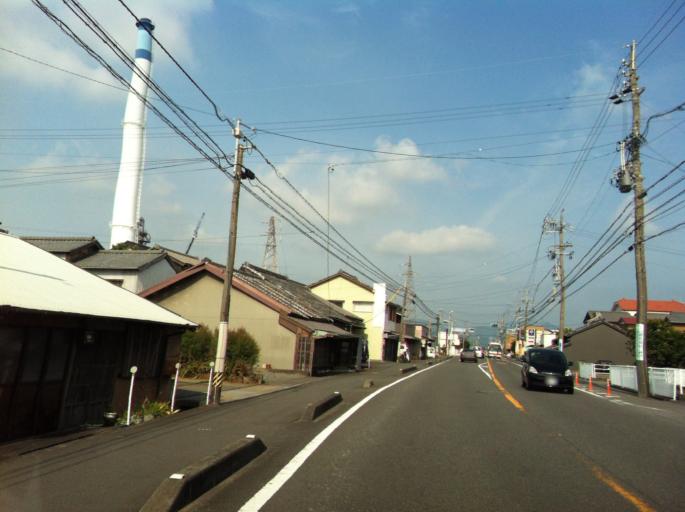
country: JP
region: Shizuoka
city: Shimada
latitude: 34.8331
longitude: 138.1636
